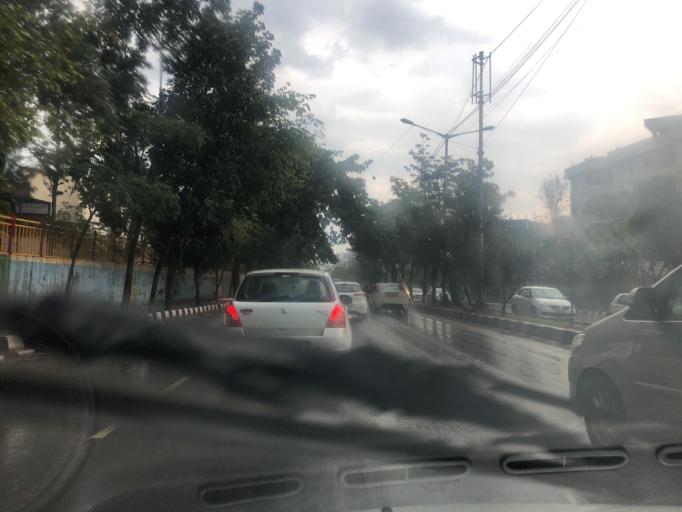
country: IN
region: Karnataka
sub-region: Bangalore Urban
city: Bangalore
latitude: 12.9699
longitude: 77.7005
